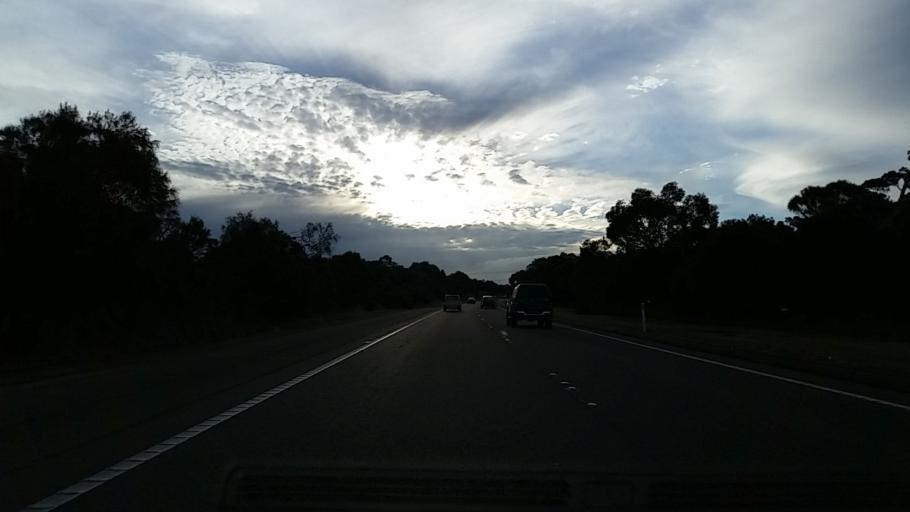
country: AU
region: South Australia
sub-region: Mount Barker
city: Nairne
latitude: -35.0829
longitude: 138.9549
